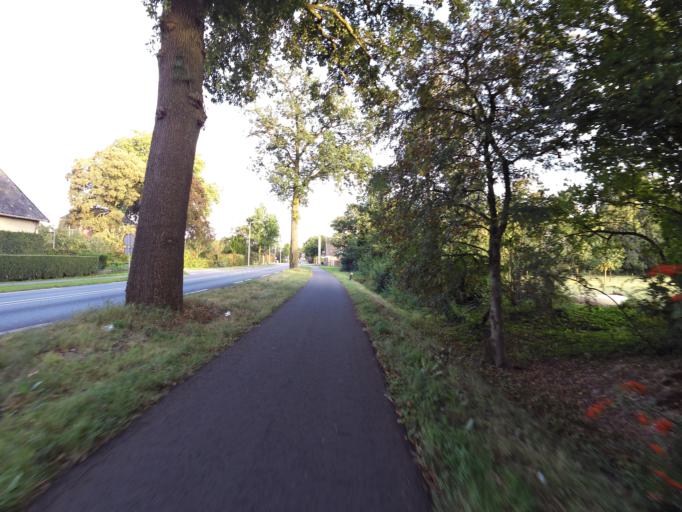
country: NL
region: Gelderland
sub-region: Gemeente Zevenaar
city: Zevenaar
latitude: 51.9132
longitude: 6.0980
